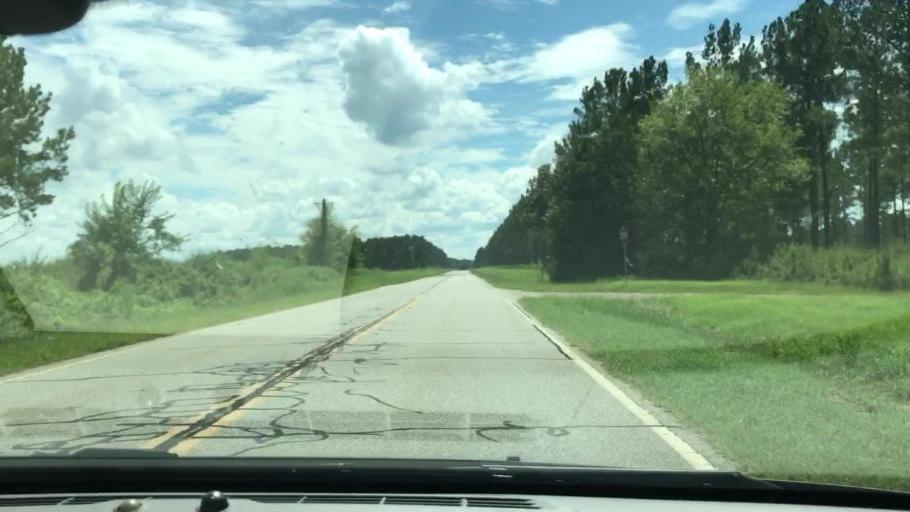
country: US
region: Georgia
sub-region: Quitman County
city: Georgetown
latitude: 32.0667
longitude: -85.0362
